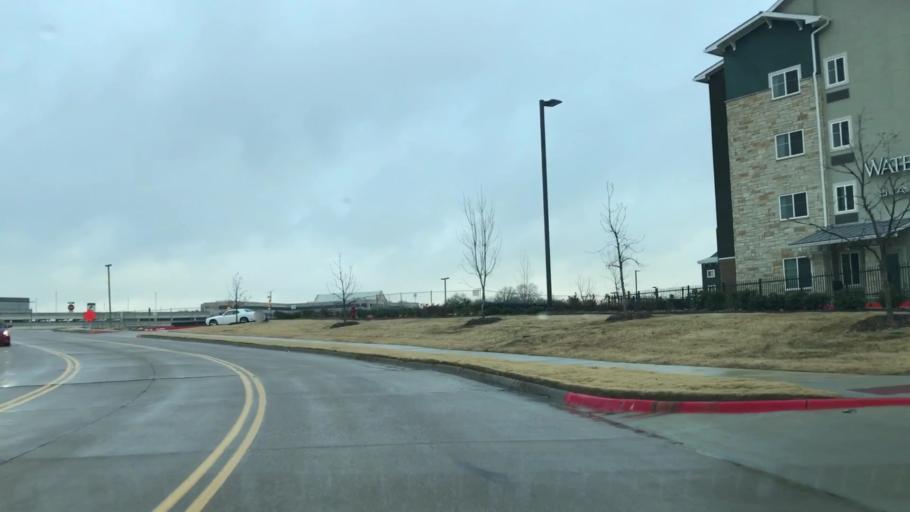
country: US
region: Texas
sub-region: Dallas County
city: Coppell
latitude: 32.9005
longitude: -96.9690
